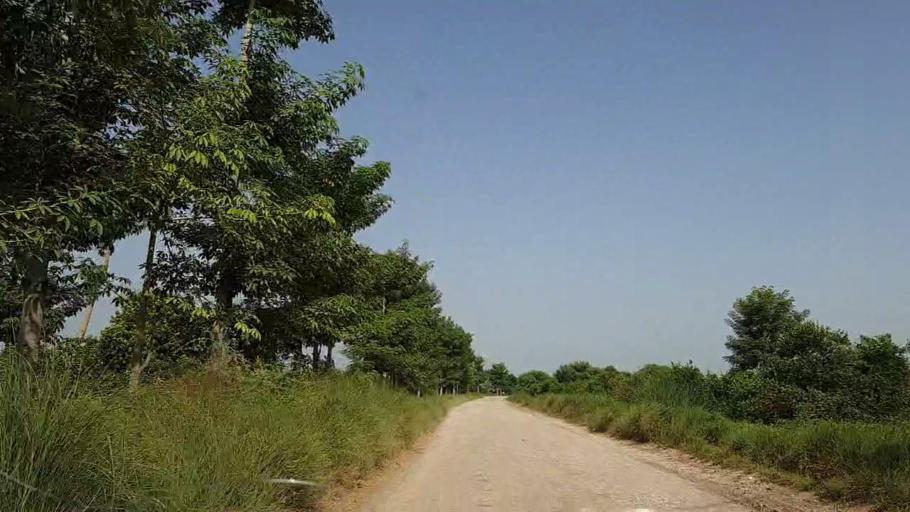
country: PK
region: Sindh
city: Kandiaro
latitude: 27.0666
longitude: 68.1784
